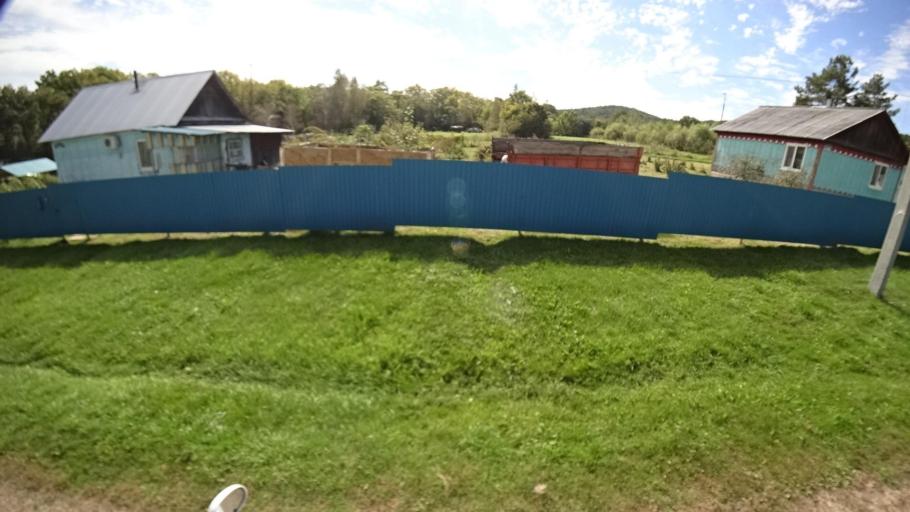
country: RU
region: Primorskiy
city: Yakovlevka
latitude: 44.3956
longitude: 133.6011
